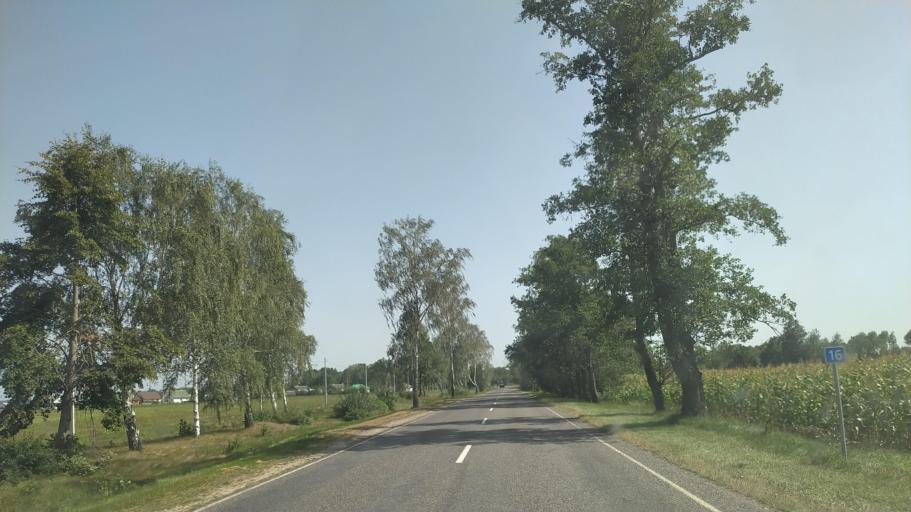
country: BY
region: Brest
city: Byaroza
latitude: 52.3935
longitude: 25.0112
